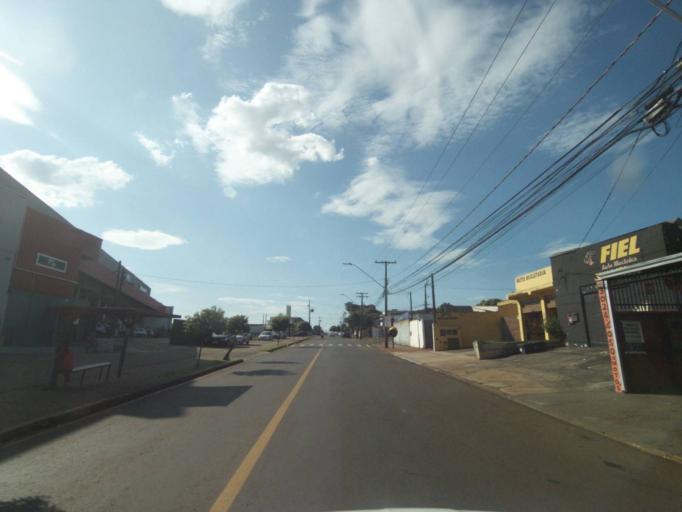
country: BR
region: Parana
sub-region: Londrina
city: Londrina
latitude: -23.3604
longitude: -51.1482
